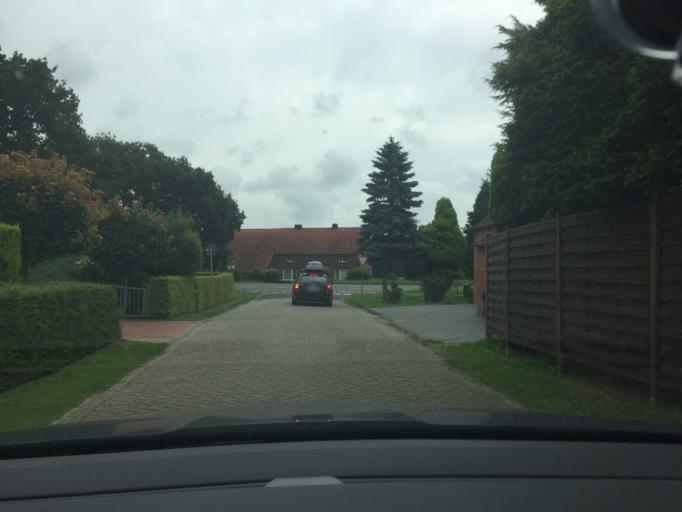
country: DE
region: Lower Saxony
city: Aurich
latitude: 53.4484
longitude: 7.5047
